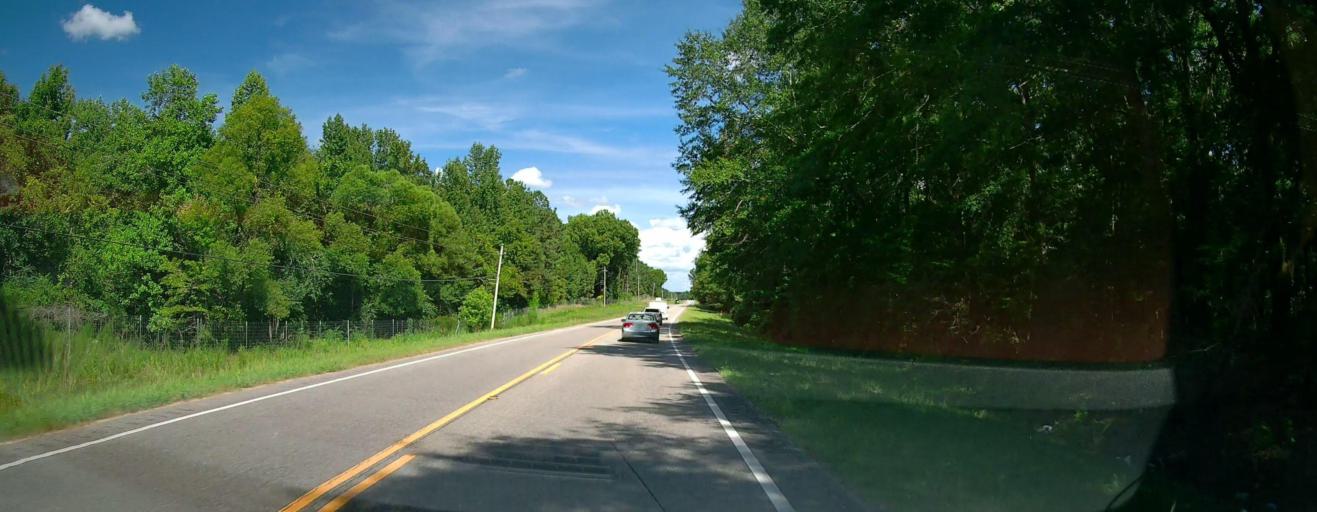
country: US
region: Alabama
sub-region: Macon County
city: Tuskegee
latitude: 32.3846
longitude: -85.8113
